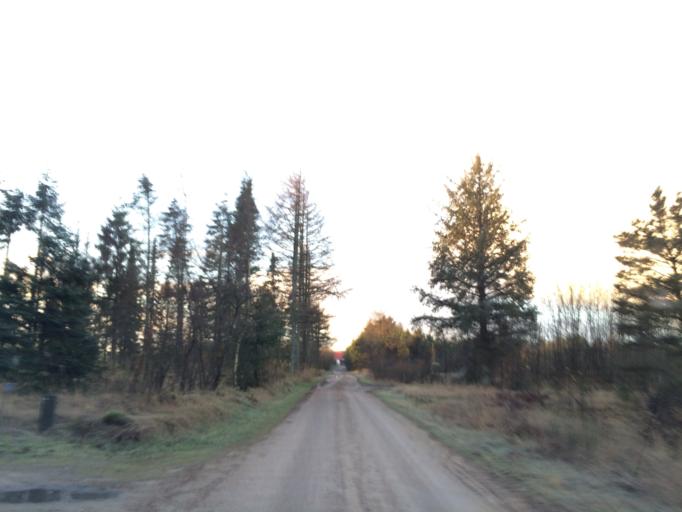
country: DK
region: Central Jutland
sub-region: Ringkobing-Skjern Kommune
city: Videbaek
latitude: 56.2119
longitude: 8.5166
